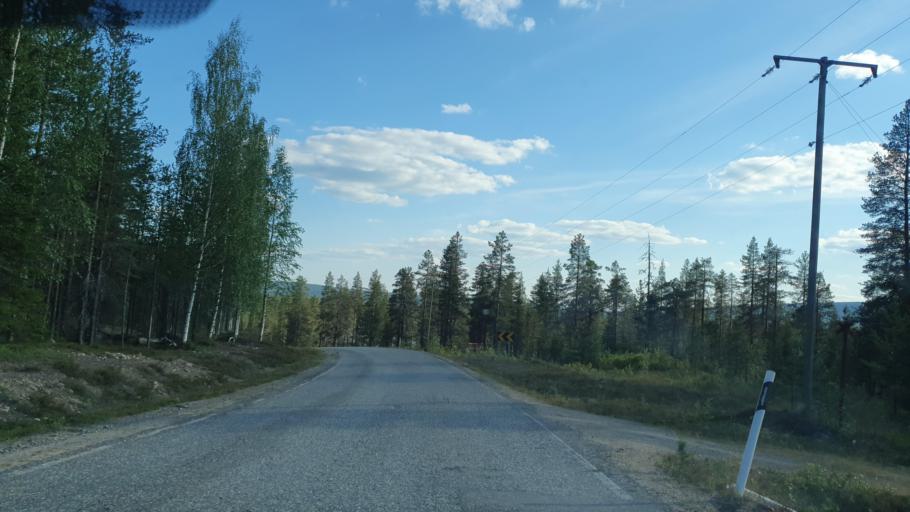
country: FI
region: Lapland
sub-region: Tunturi-Lappi
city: Kolari
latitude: 67.6378
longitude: 24.1565
